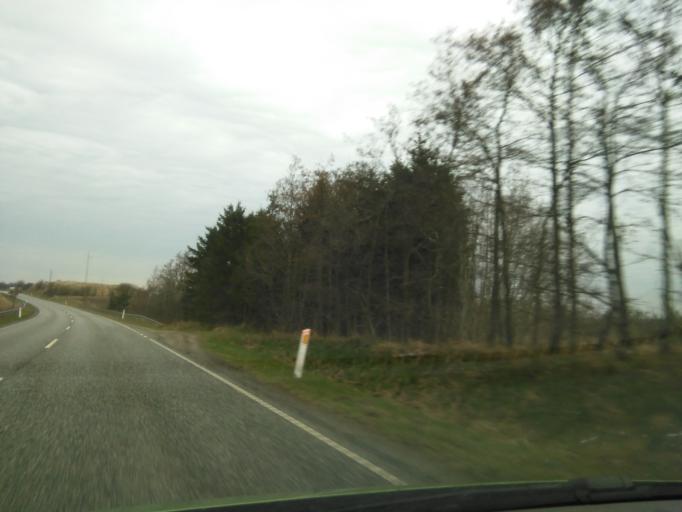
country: DK
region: North Denmark
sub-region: Mariagerfjord Kommune
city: Hadsund
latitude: 56.6783
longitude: 10.0768
